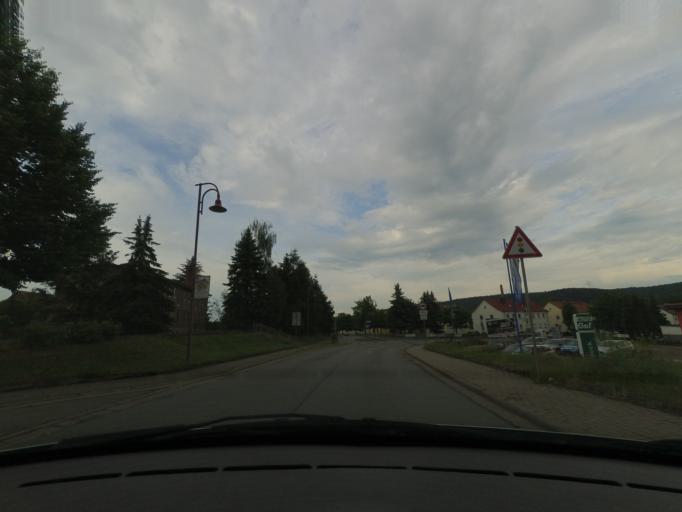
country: DE
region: Thuringia
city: Stadtilm
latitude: 50.7780
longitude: 11.0827
